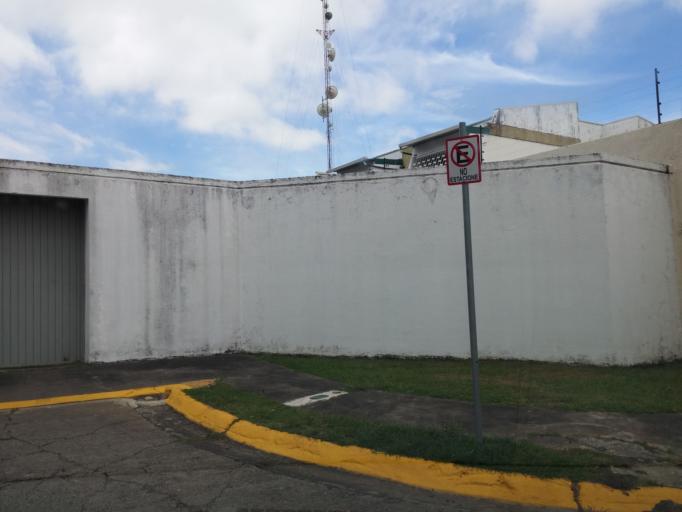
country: CR
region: San Jose
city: Colima
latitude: 9.9405
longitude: -84.1085
